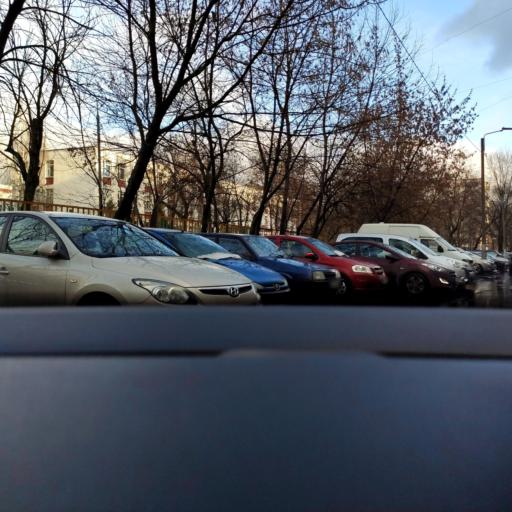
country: RU
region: Moscow
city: Bibirevo
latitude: 55.8903
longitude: 37.6003
